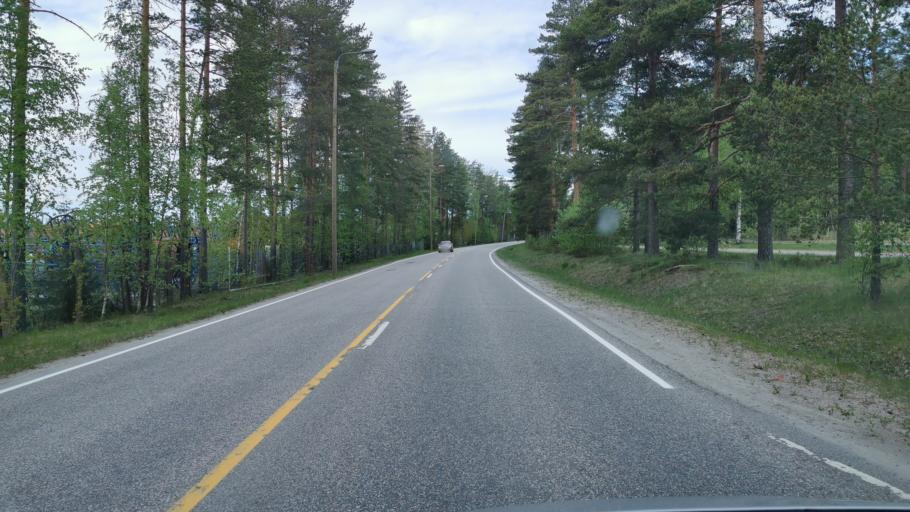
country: FI
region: Paijanne Tavastia
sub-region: Lahti
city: Nastola
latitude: 60.9334
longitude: 25.9659
